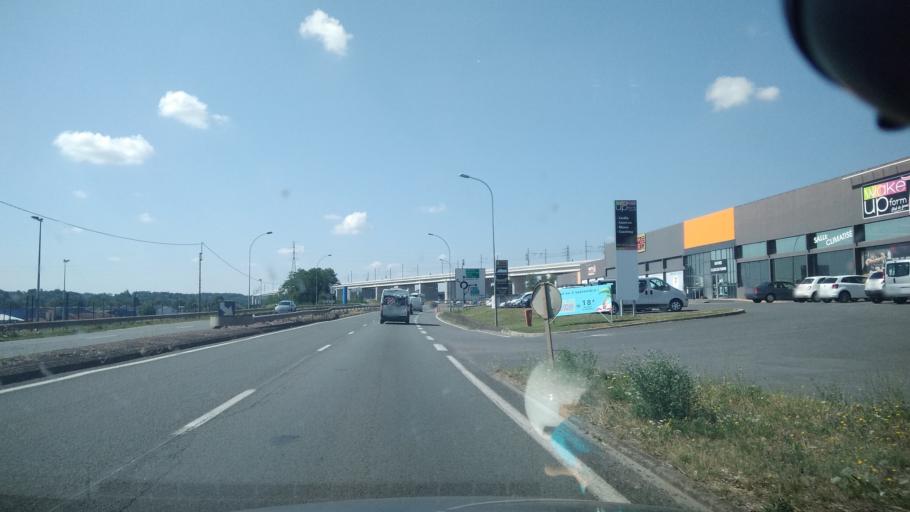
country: FR
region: Poitou-Charentes
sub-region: Departement de la Vienne
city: Chasseneuil-du-Poitou
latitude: 46.6252
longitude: 0.3541
